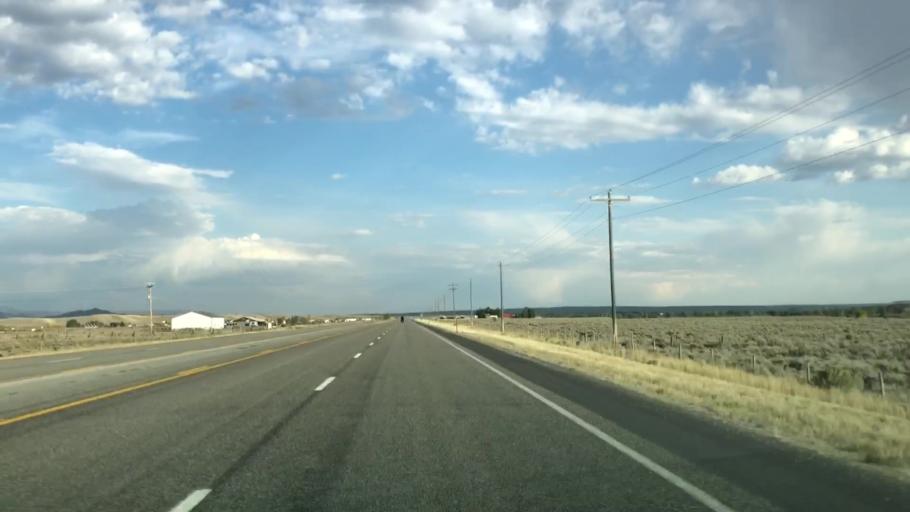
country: US
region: Wyoming
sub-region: Sublette County
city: Pinedale
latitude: 42.7813
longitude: -109.7648
